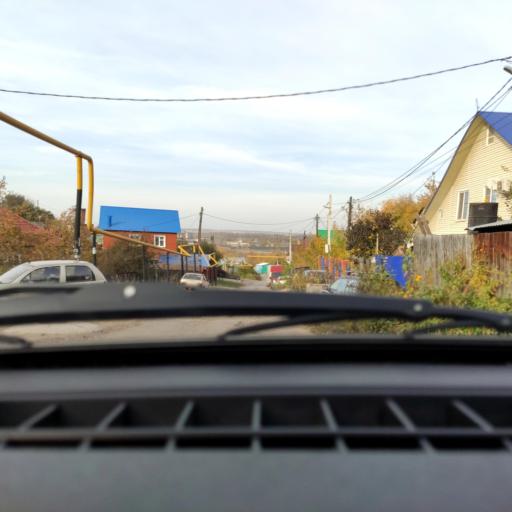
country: RU
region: Bashkortostan
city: Ufa
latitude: 54.7361
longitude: 55.9264
